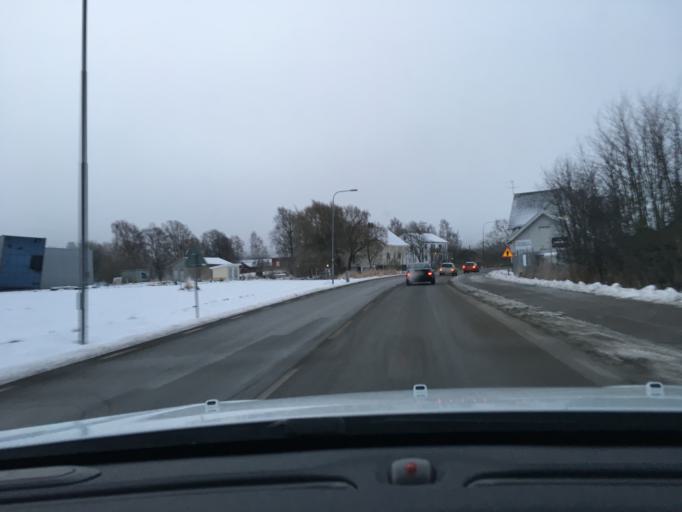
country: SE
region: Vaestra Goetaland
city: Svanesund
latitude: 58.1056
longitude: 11.8513
